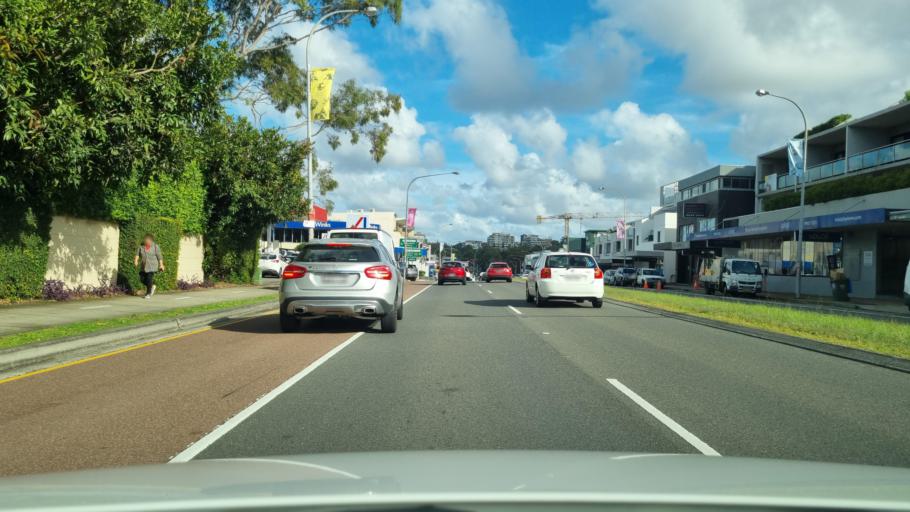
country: AU
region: New South Wales
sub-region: Warringah
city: North Manly
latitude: -33.7846
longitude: 151.2673
